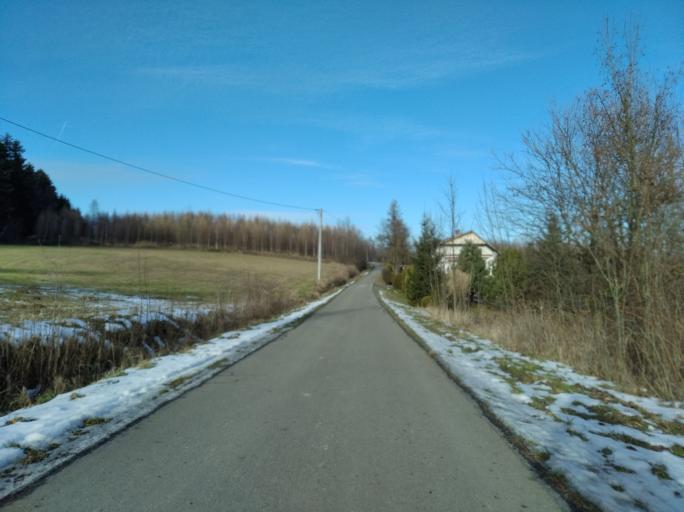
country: PL
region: Subcarpathian Voivodeship
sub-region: Powiat strzyzowski
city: Gwoznica Gorna
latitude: 49.8170
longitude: 21.9900
